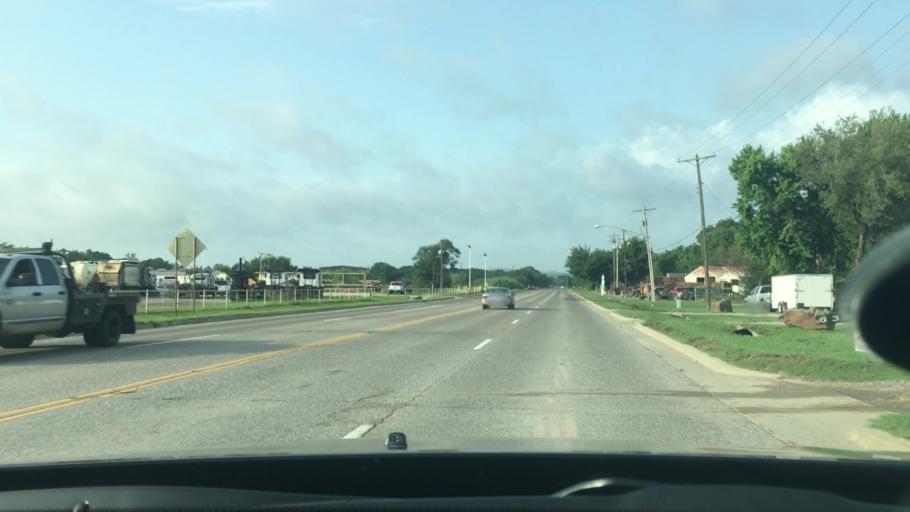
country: US
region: Oklahoma
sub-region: Murray County
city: Davis
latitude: 34.4973
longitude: -97.1262
